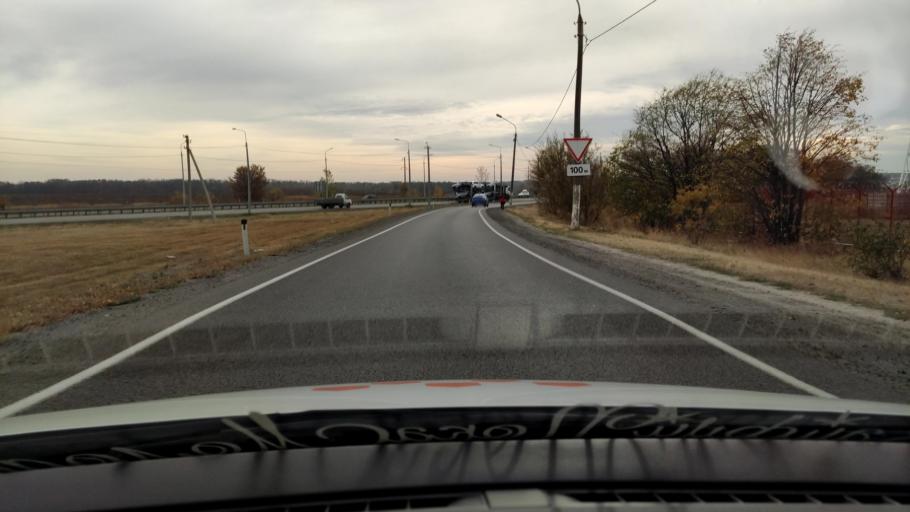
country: RU
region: Voronezj
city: Ramon'
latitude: 51.9279
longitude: 39.2194
